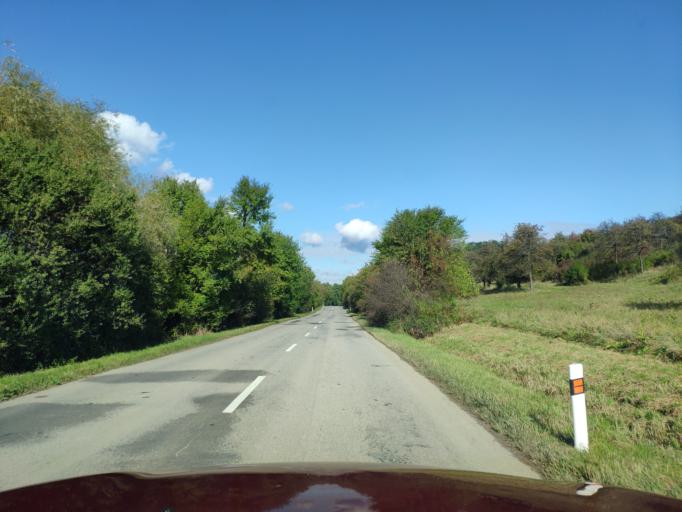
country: SK
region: Presovsky
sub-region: Okres Presov
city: Presov
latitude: 48.8820
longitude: 21.2667
